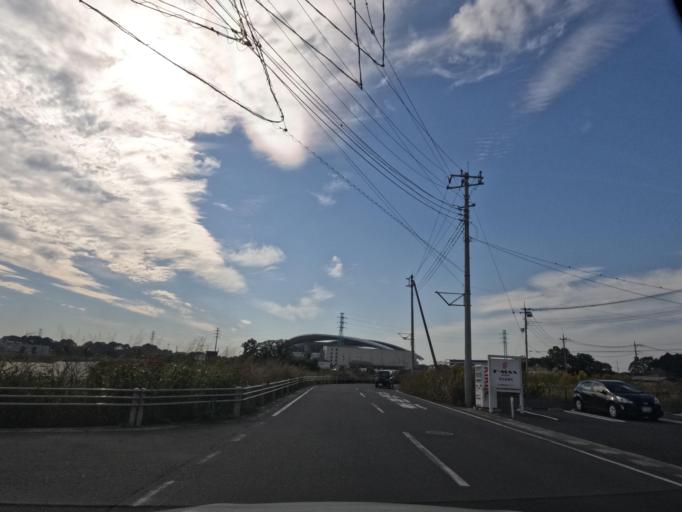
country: JP
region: Saitama
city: Iwatsuki
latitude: 35.9057
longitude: 139.7256
